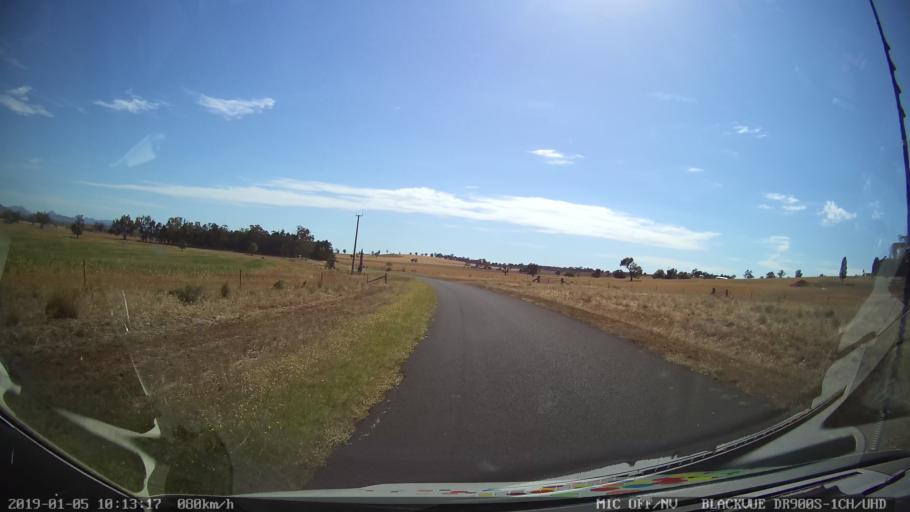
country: AU
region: New South Wales
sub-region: Gilgandra
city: Gilgandra
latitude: -31.6033
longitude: 148.9230
